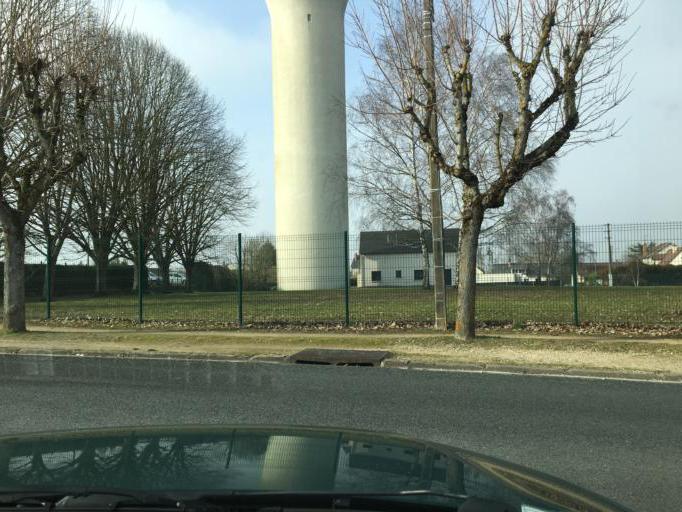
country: FR
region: Centre
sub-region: Departement du Loiret
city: Beaugency
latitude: 47.7741
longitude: 1.6252
